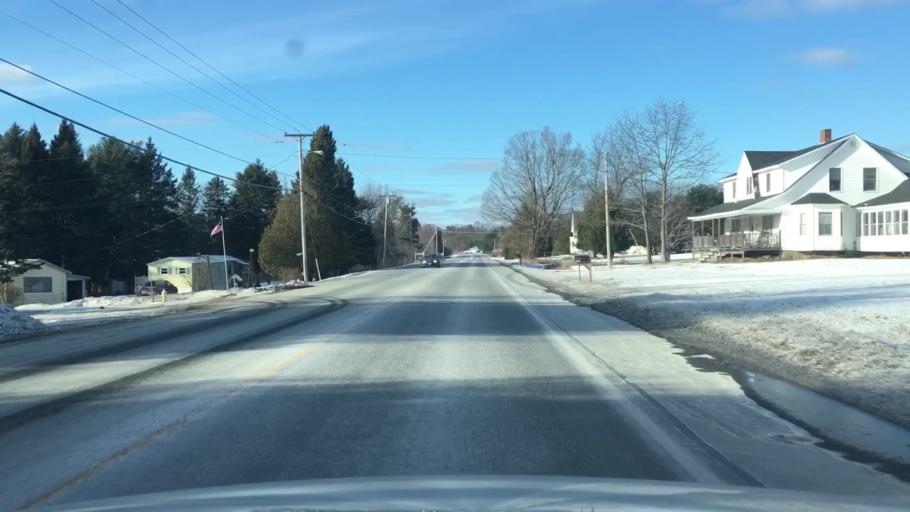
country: US
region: Maine
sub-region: Penobscot County
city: Holden
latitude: 44.7980
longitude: -68.5938
